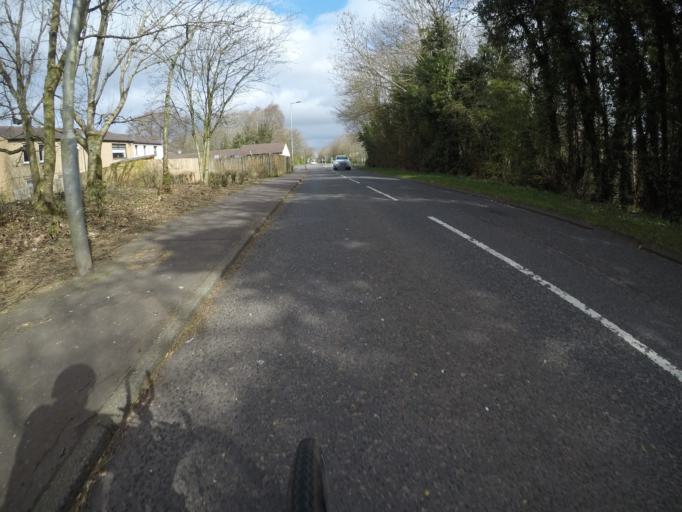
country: GB
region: Scotland
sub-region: North Ayrshire
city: Irvine
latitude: 55.6306
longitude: -4.6363
